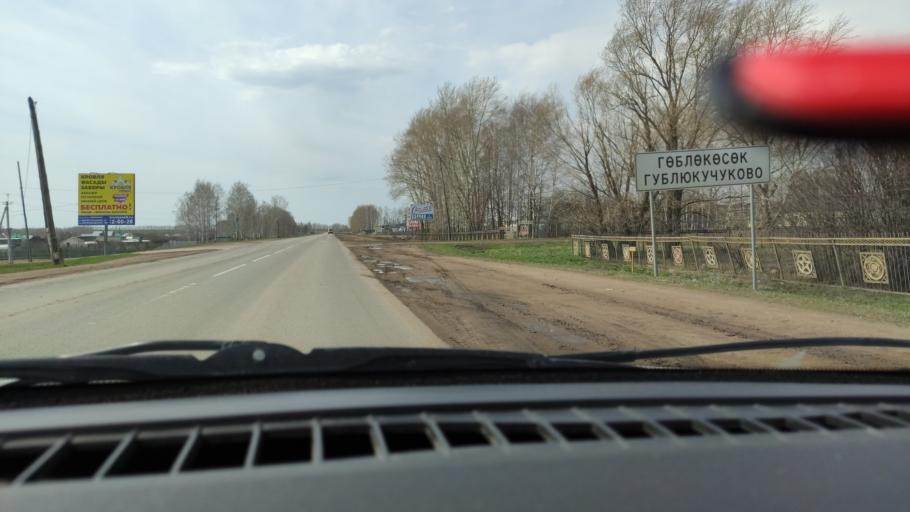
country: RU
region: Bashkortostan
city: Dyurtyuli
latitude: 55.4913
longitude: 54.8027
